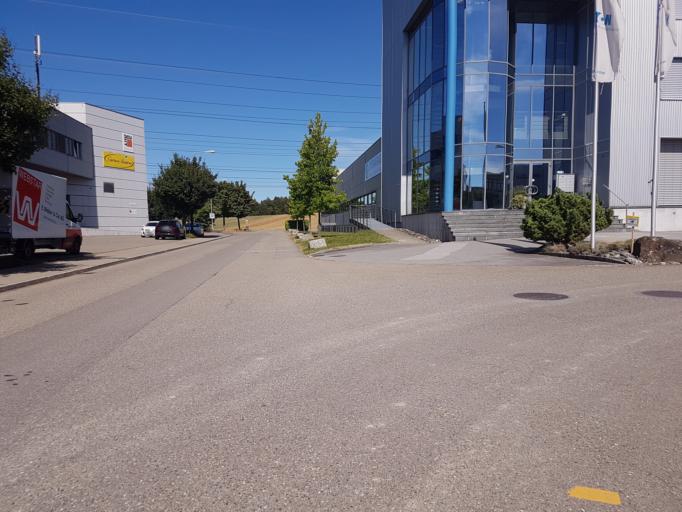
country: CH
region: Zurich
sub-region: Bezirk Pfaeffikon
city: Effretikon
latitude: 47.4391
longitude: 8.6878
